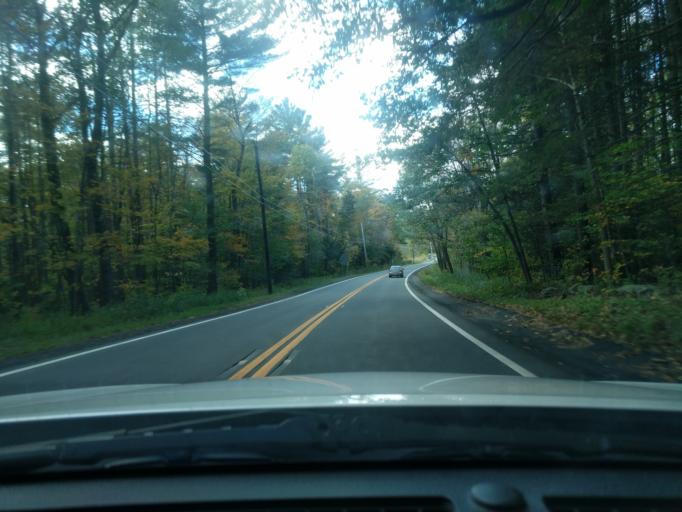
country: US
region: Massachusetts
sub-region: Berkshire County
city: Otis
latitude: 42.1928
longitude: -73.1226
